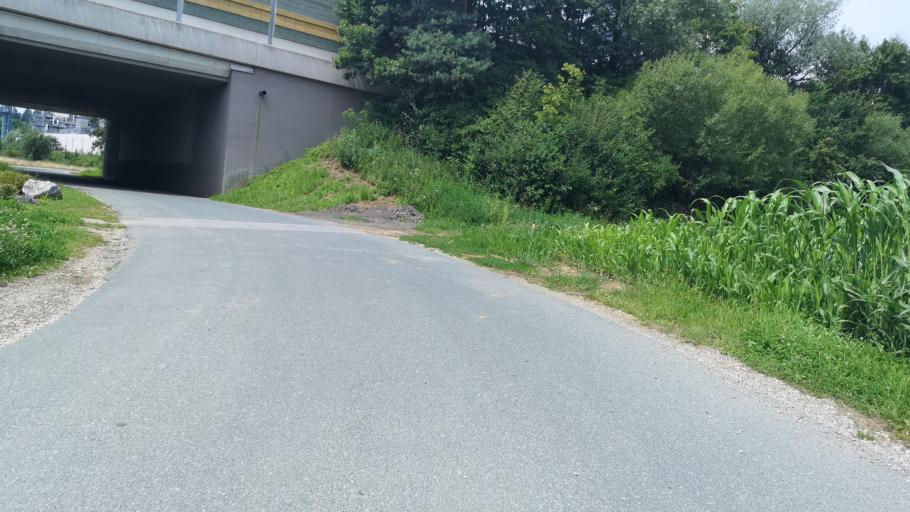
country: AT
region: Styria
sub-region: Politischer Bezirk Leibnitz
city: Weitendorf
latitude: 46.8811
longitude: 15.4768
